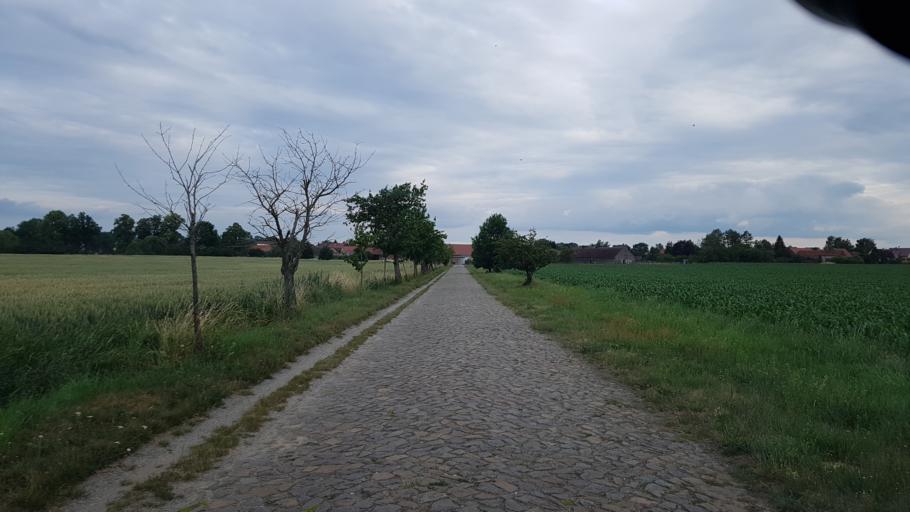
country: DE
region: Brandenburg
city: Schlieben
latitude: 51.7256
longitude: 13.4189
